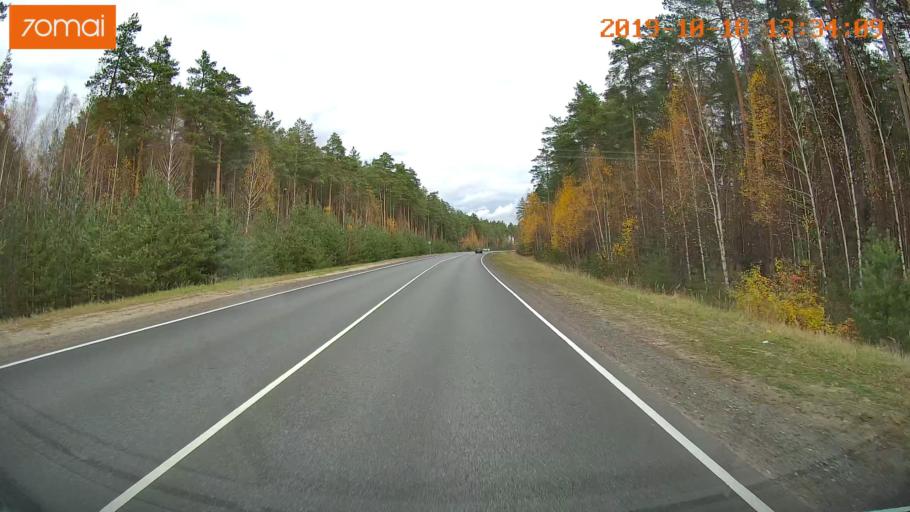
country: RU
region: Rjazan
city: Solotcha
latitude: 54.8520
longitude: 39.9482
